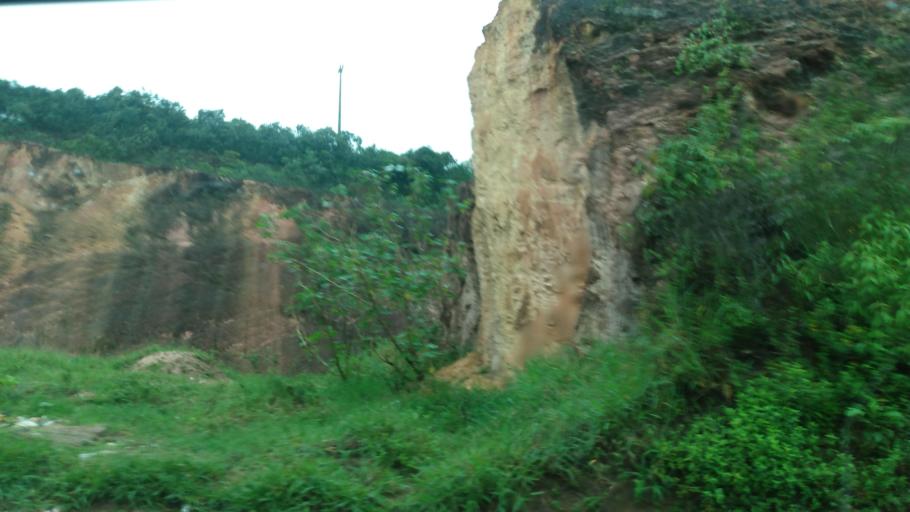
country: BR
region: Pernambuco
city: Garanhuns
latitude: -8.8776
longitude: -36.5099
